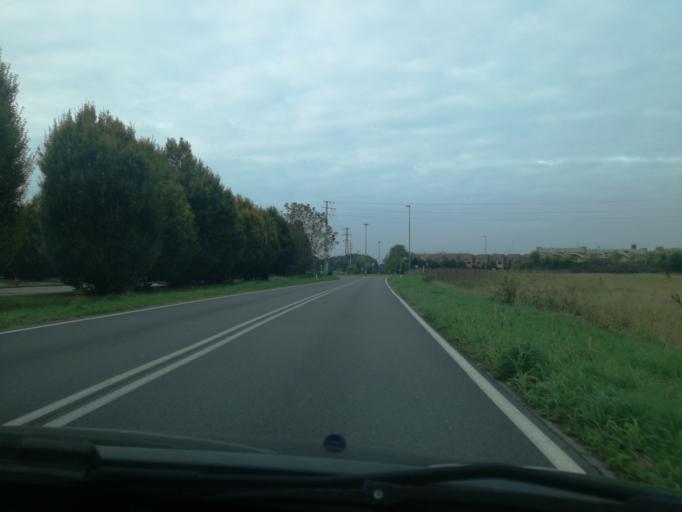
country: IT
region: Lombardy
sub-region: Provincia di Monza e Brianza
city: Bellusco
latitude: 45.6275
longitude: 9.4150
